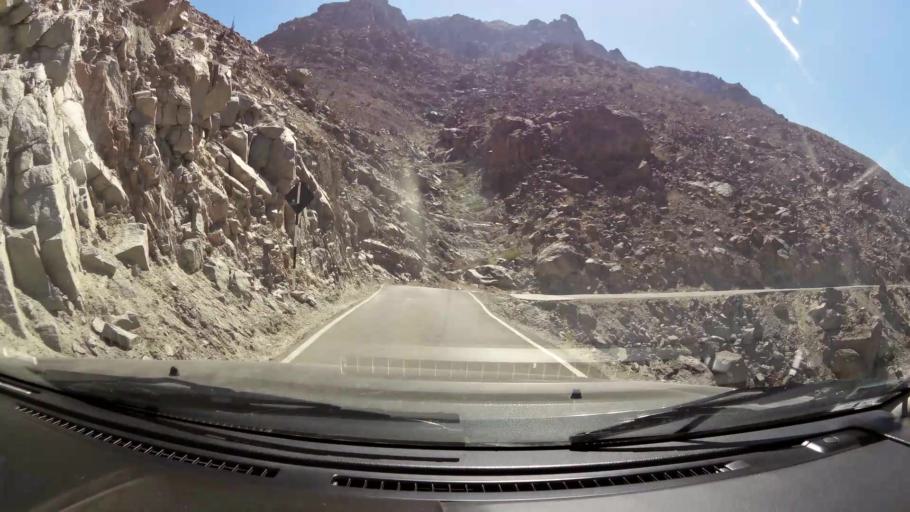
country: PE
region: Ica
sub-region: Provincia de Ica
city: La Tinguina
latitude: -13.8377
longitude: -75.5566
